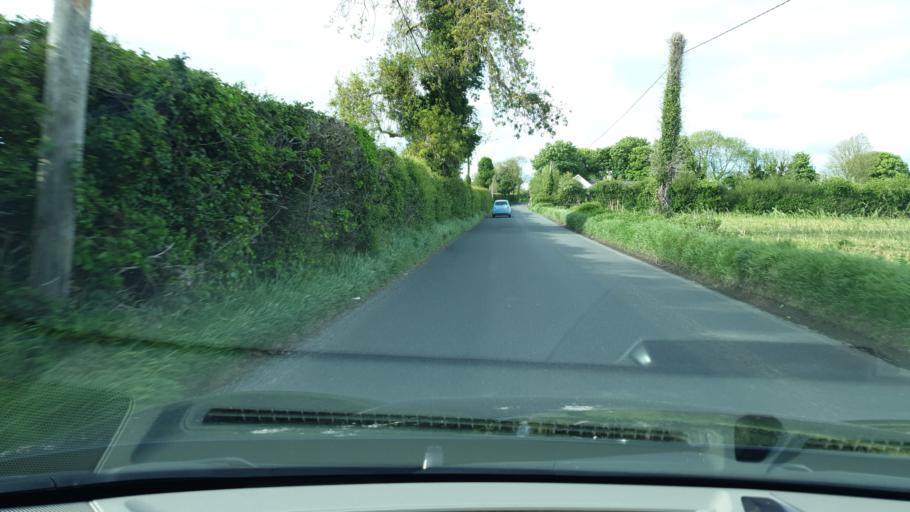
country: IE
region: Leinster
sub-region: An Mhi
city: Ashbourne
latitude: 53.5303
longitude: -6.4074
